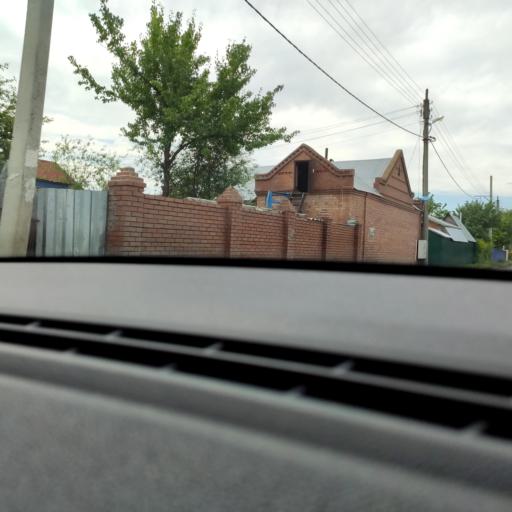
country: RU
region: Samara
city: Podstepki
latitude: 53.5086
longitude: 49.1747
